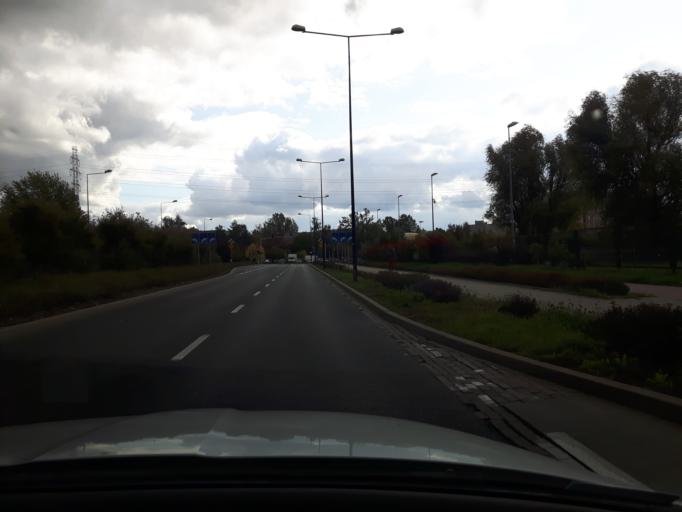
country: PL
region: Masovian Voivodeship
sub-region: Warszawa
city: Ursynow
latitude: 52.1602
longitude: 21.0501
